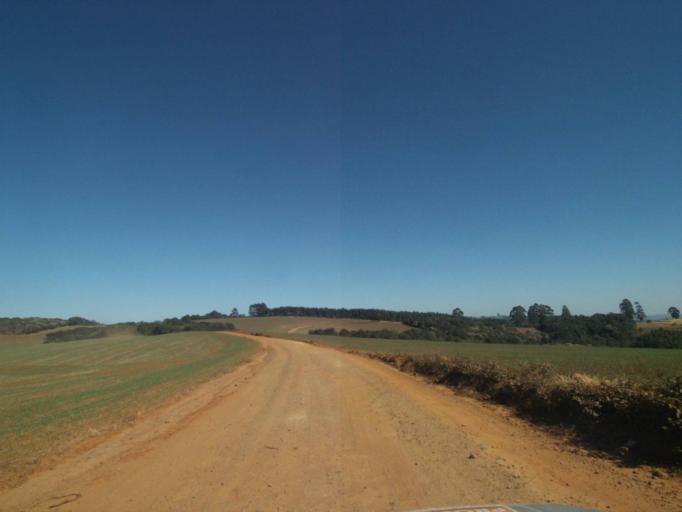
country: BR
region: Parana
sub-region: Tibagi
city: Tibagi
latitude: -24.5637
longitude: -50.6257
